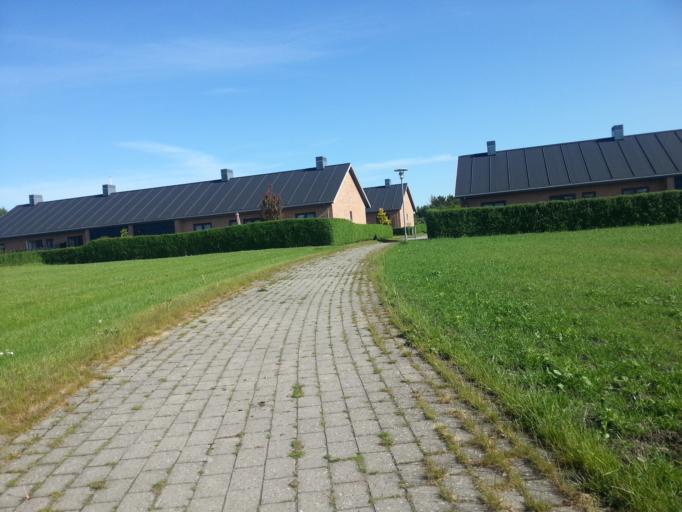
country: DK
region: North Denmark
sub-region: Alborg Kommune
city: Vadum
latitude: 57.1232
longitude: 9.8648
